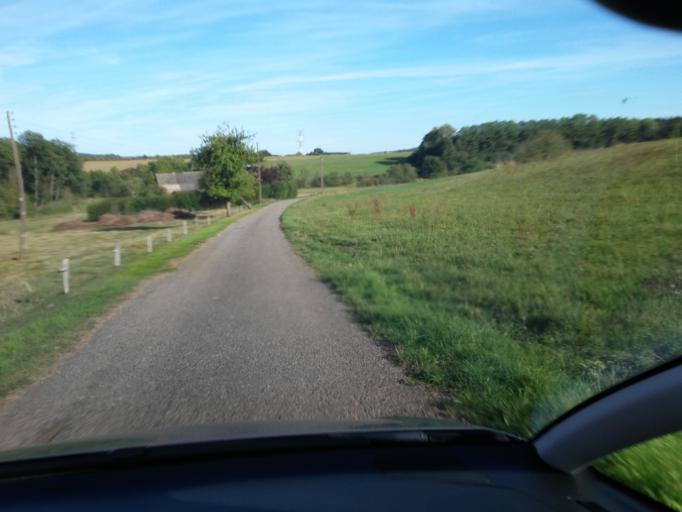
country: BE
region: Wallonia
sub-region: Province du Luxembourg
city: Habay-la-Vieille
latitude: 49.7076
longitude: 5.7028
